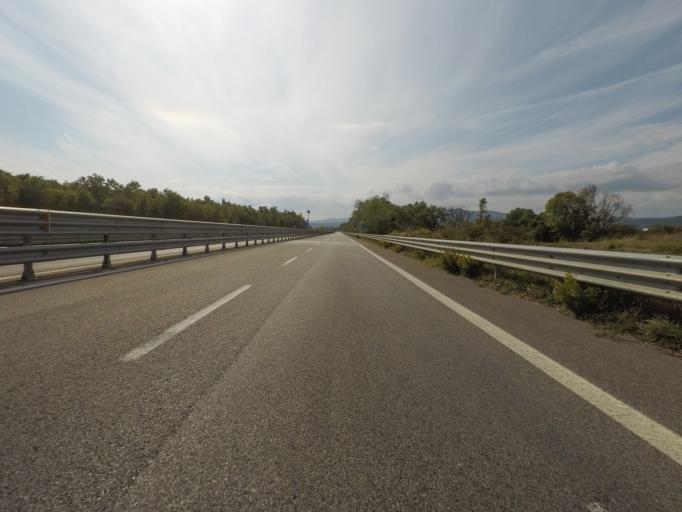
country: IT
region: Tuscany
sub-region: Provincia di Siena
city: Rosia
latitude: 43.2273
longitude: 11.2750
